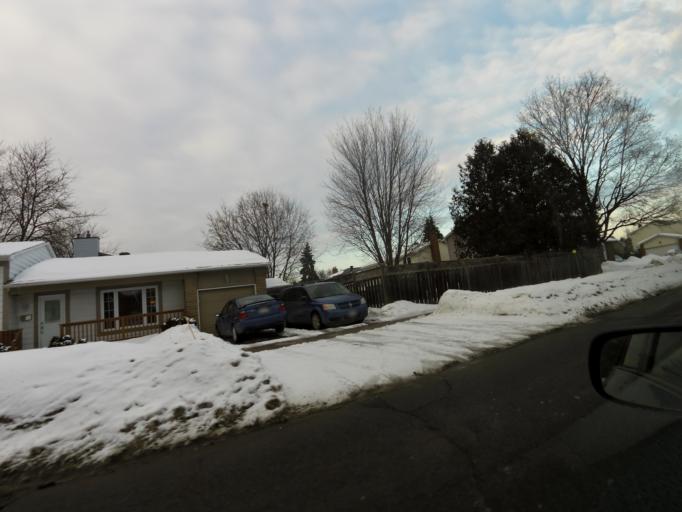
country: CA
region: Quebec
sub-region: Outaouais
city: Gatineau
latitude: 45.4714
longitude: -75.5424
